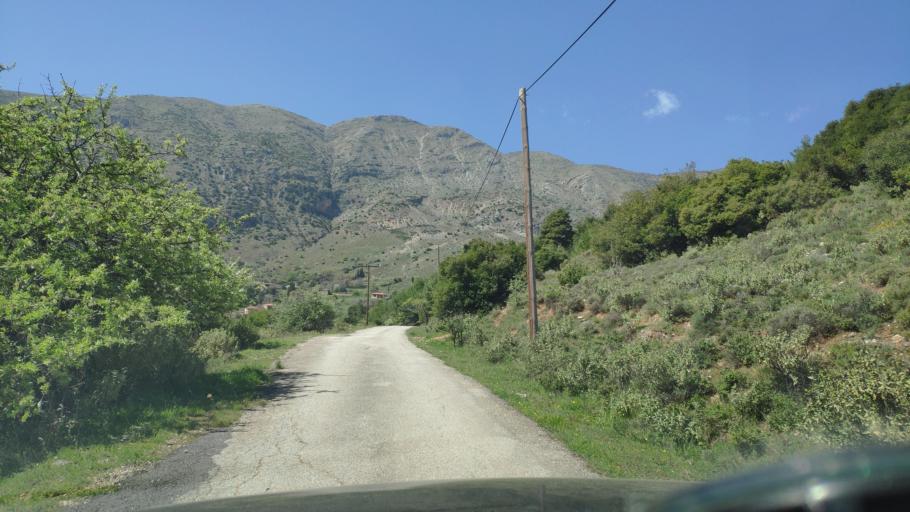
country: GR
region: West Greece
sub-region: Nomos Achaias
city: Akrata
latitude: 38.0754
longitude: 22.3210
